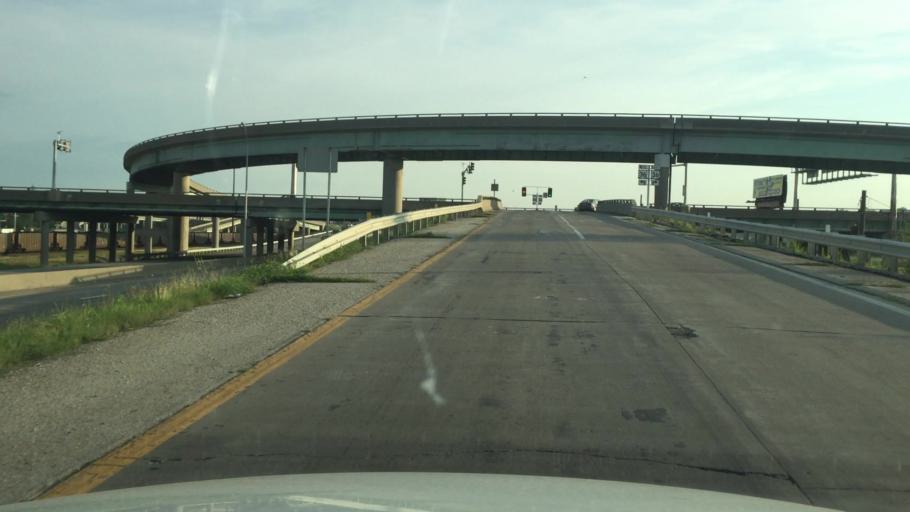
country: US
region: Kansas
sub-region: Doniphan County
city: Elwood
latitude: 39.7478
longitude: -94.8533
